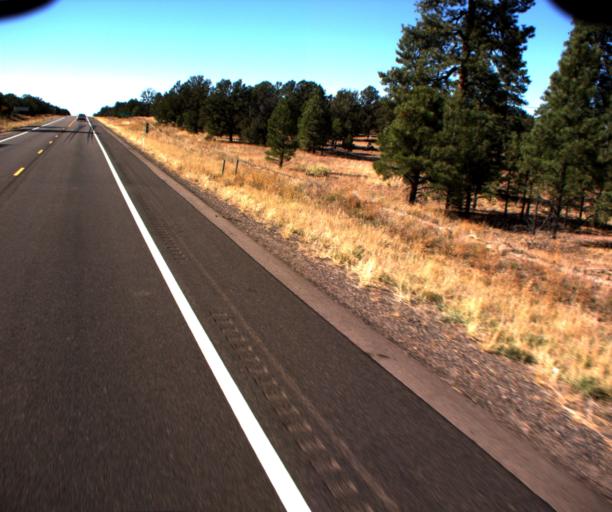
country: US
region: Arizona
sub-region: Apache County
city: Saint Michaels
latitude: 35.7019
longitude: -109.2965
